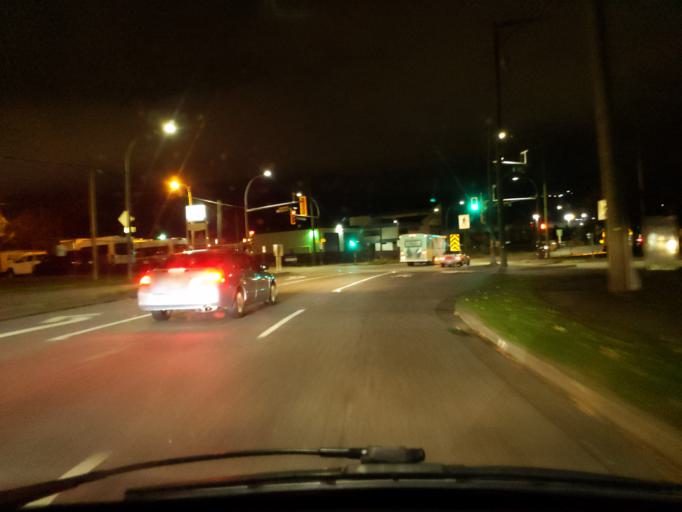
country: CA
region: British Columbia
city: Burnaby
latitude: 49.2604
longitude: -123.0137
